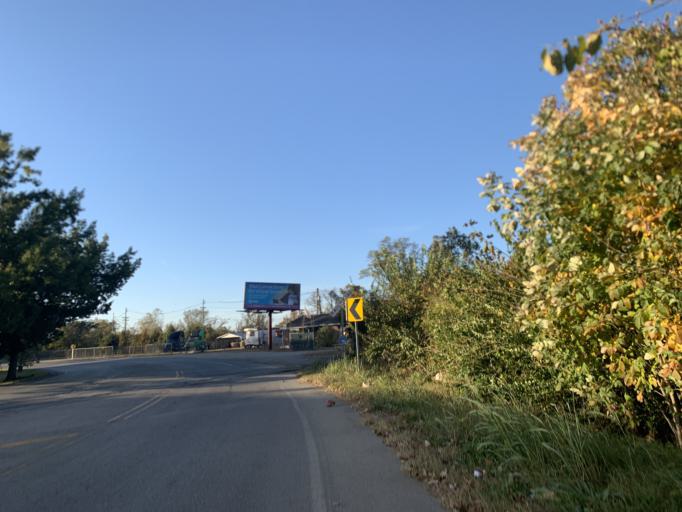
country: US
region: Kentucky
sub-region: Jefferson County
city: Shively
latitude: 38.2319
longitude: -85.8275
